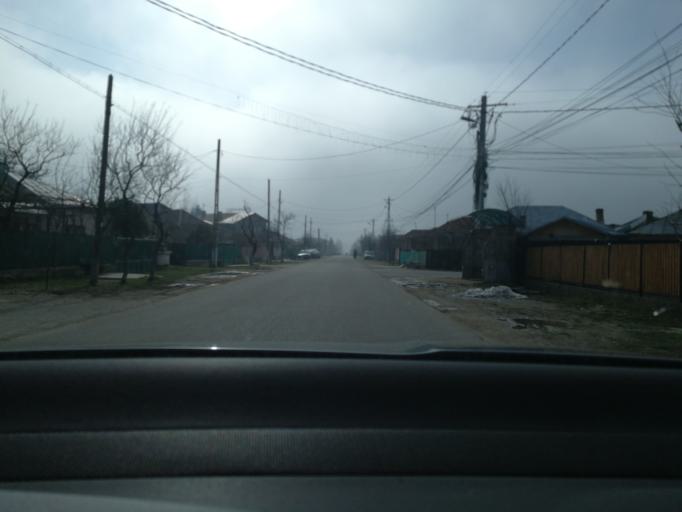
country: RO
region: Prahova
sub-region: Comuna Magureni
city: Lunca Prahovei
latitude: 45.0371
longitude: 25.7593
